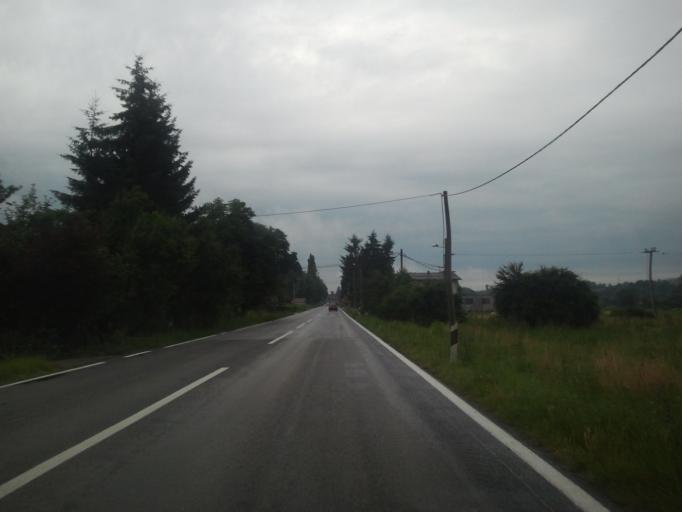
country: HR
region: Karlovacka
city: Vojnic
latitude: 45.3871
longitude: 15.6143
